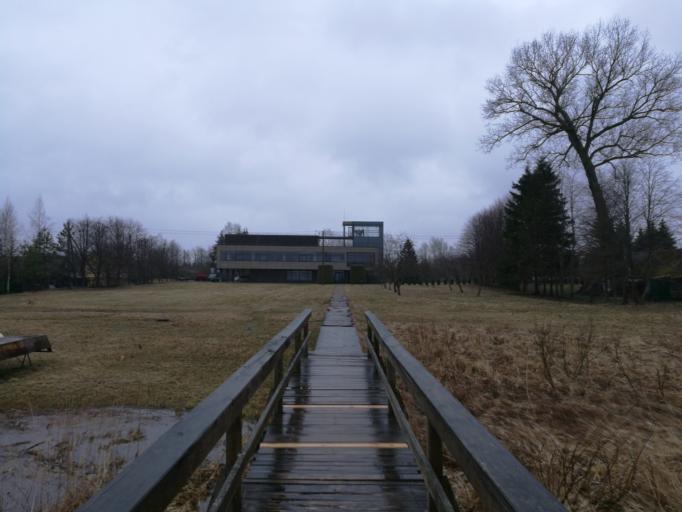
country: LT
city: Simnas
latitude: 54.4573
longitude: 23.6386
